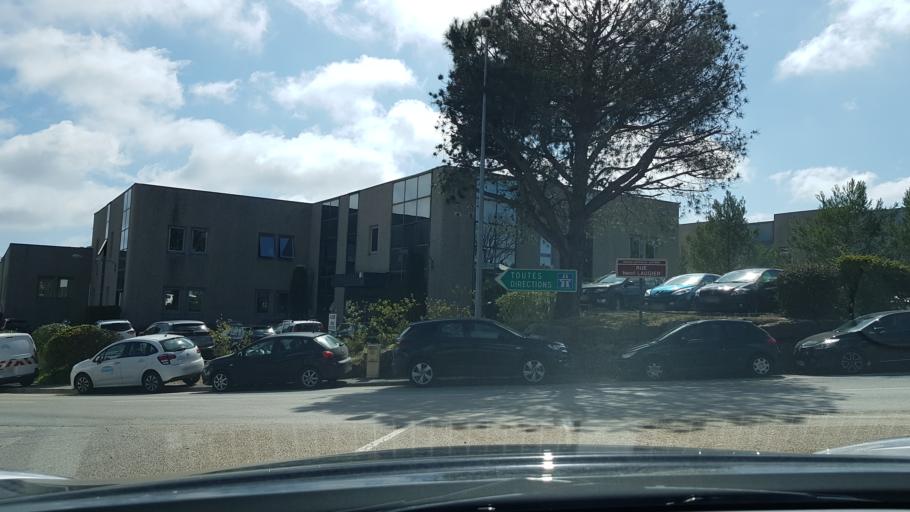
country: FR
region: Provence-Alpes-Cote d'Azur
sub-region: Departement des Alpes-Maritimes
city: Biot
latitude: 43.6071
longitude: 7.0754
